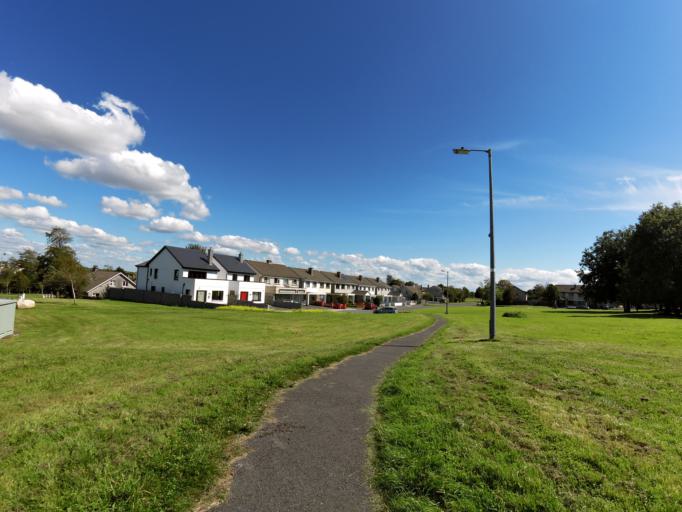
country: IE
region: Connaught
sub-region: County Galway
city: Gaillimh
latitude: 53.2863
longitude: -9.0768
